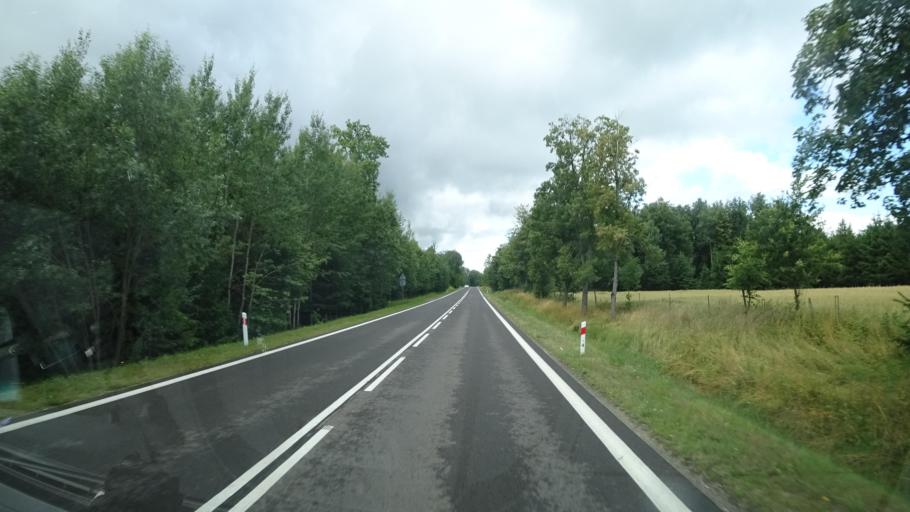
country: PL
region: Warmian-Masurian Voivodeship
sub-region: Powiat goldapski
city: Goldap
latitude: 54.2580
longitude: 22.3727
